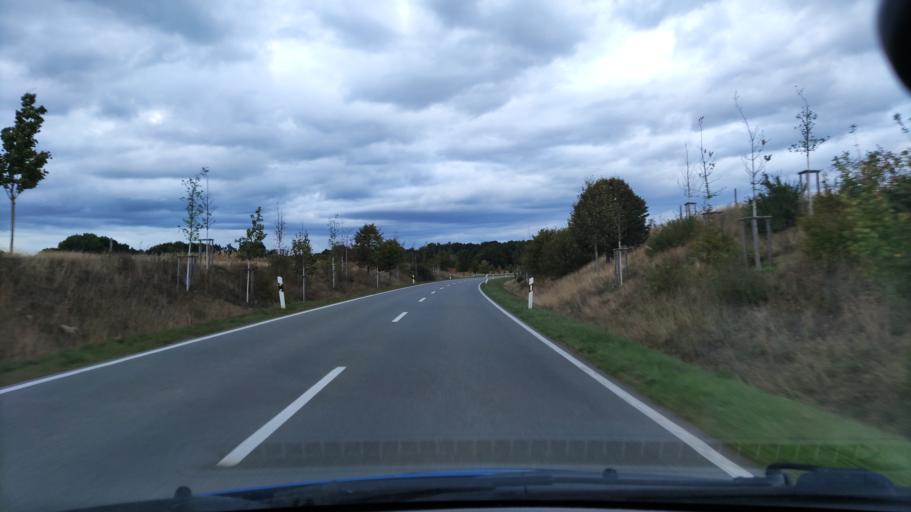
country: DE
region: Mecklenburg-Vorpommern
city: Lubtheen
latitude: 53.3695
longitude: 10.9636
